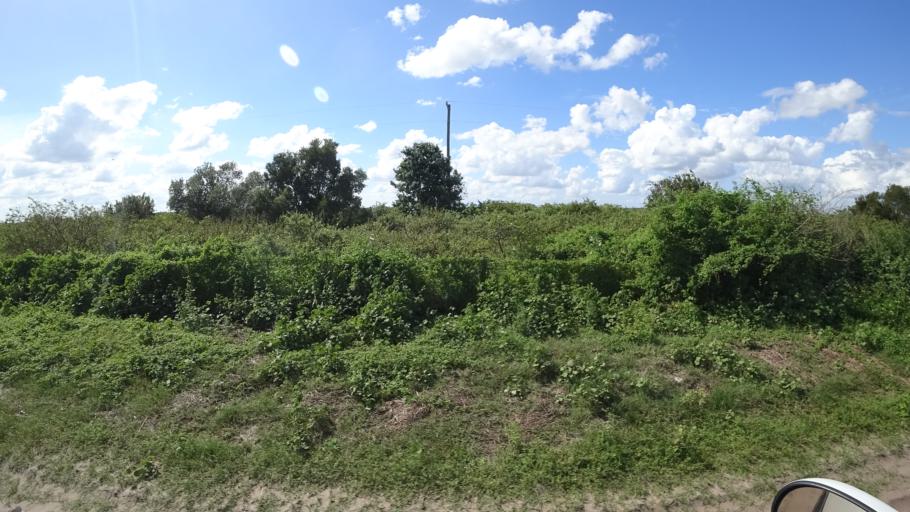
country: US
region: Florida
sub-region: DeSoto County
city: Arcadia
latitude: 27.3402
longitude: -82.0968
